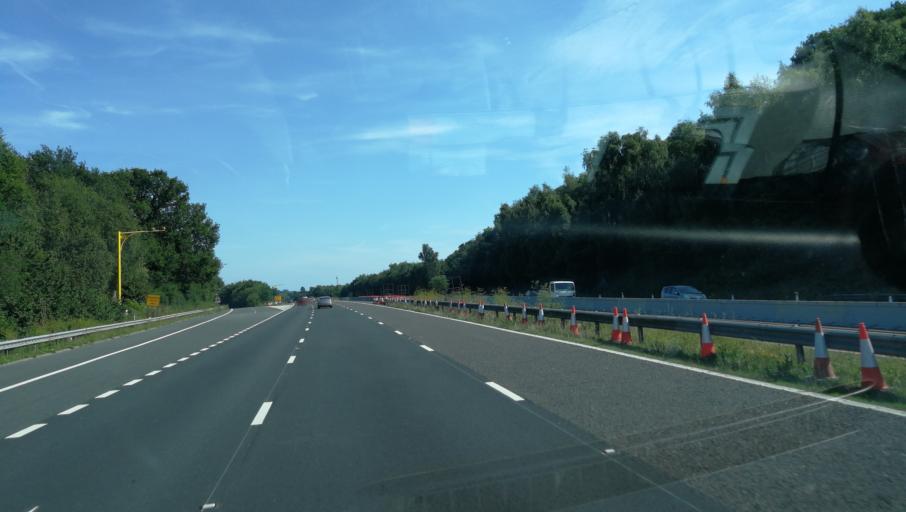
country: GB
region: England
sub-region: Kent
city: Ashford
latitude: 51.1642
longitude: 0.8620
